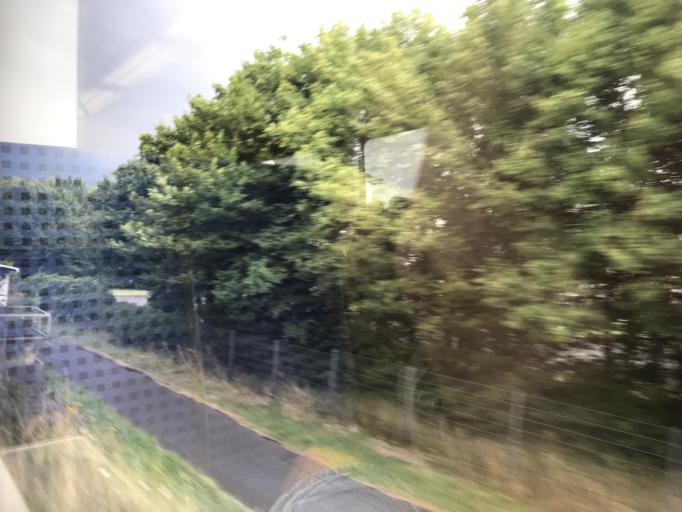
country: DE
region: North Rhine-Westphalia
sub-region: Regierungsbezirk Koln
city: Stossdorf
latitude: 50.7807
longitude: 7.2349
